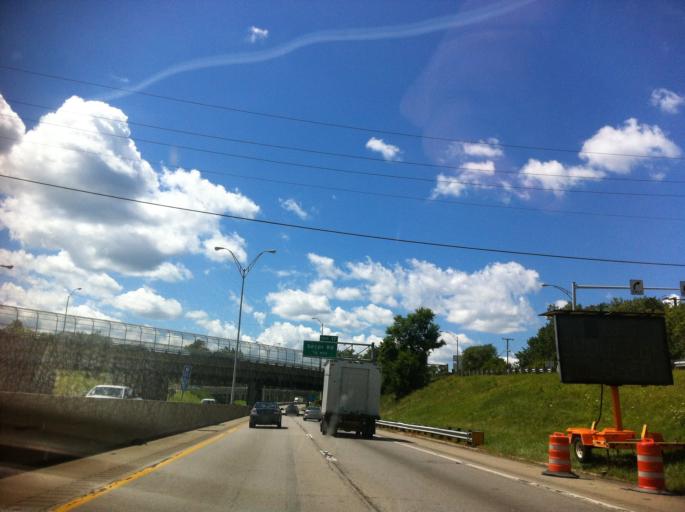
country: US
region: Ohio
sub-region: Lucas County
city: Ottawa Hills
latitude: 41.6856
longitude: -83.6130
